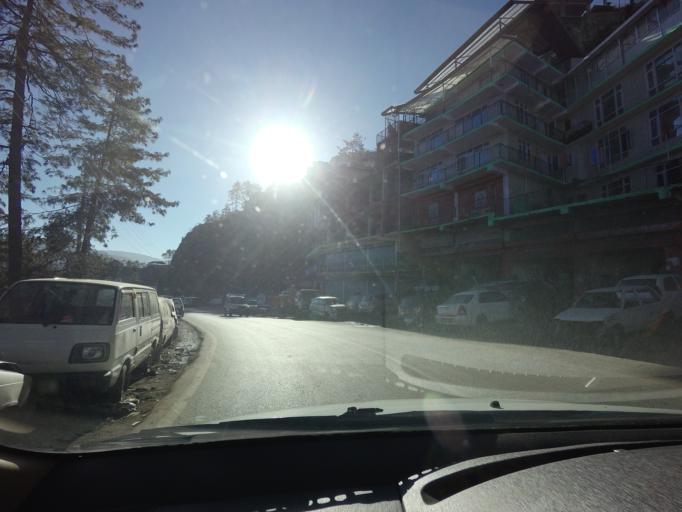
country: IN
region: Himachal Pradesh
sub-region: Shimla
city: Shimla
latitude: 31.1086
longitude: 77.2076
